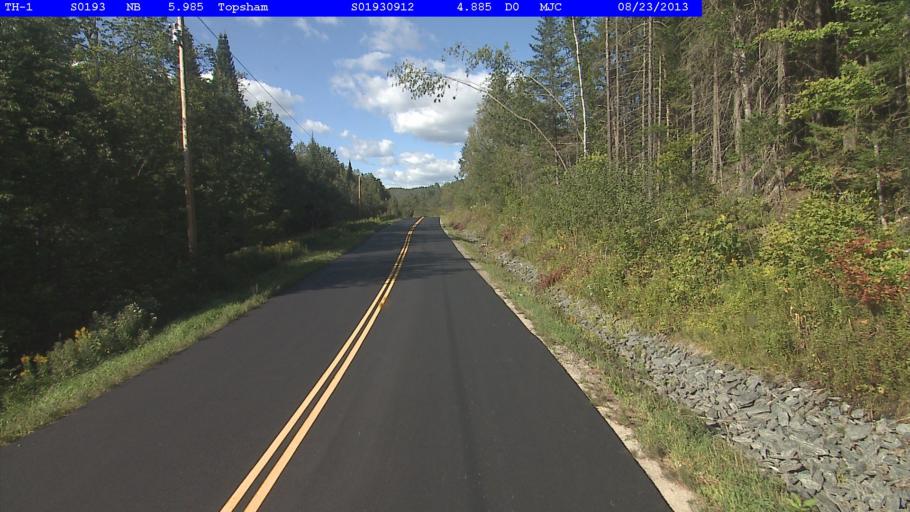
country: US
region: New Hampshire
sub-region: Grafton County
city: Haverhill
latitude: 44.1334
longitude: -72.2413
